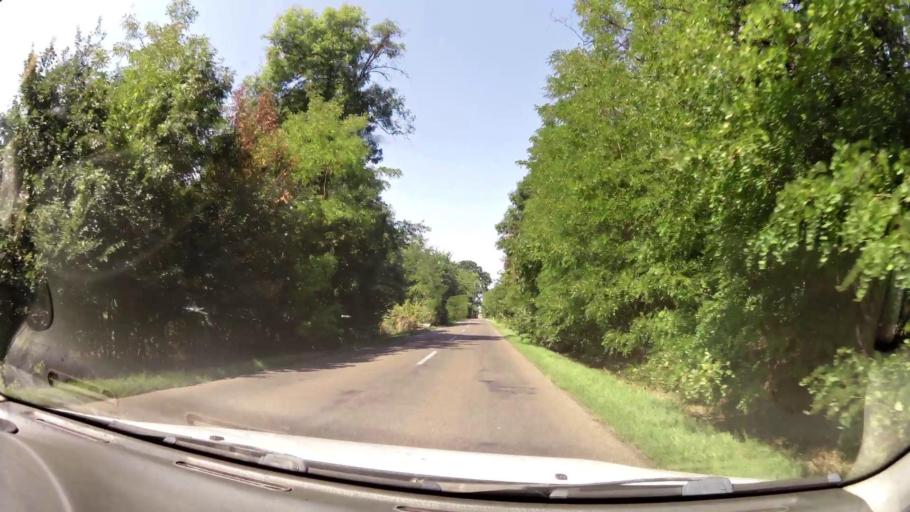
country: HU
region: Pest
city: Tapiosag
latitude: 47.3924
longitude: 19.6409
